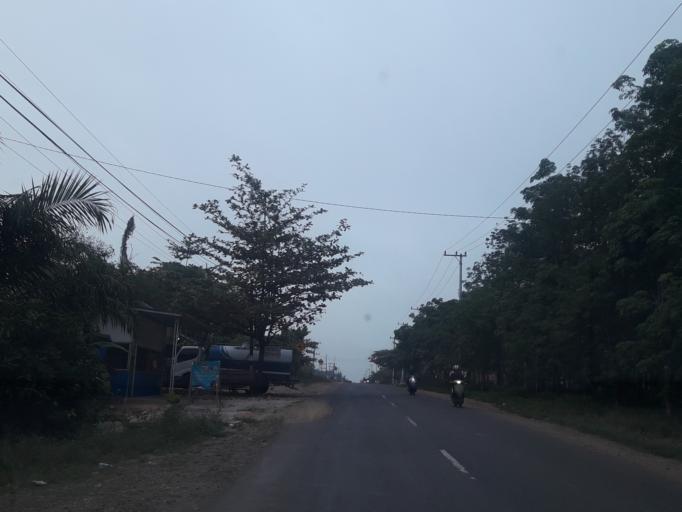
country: ID
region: South Kalimantan
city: Tanjung
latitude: -2.1337
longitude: 115.4528
